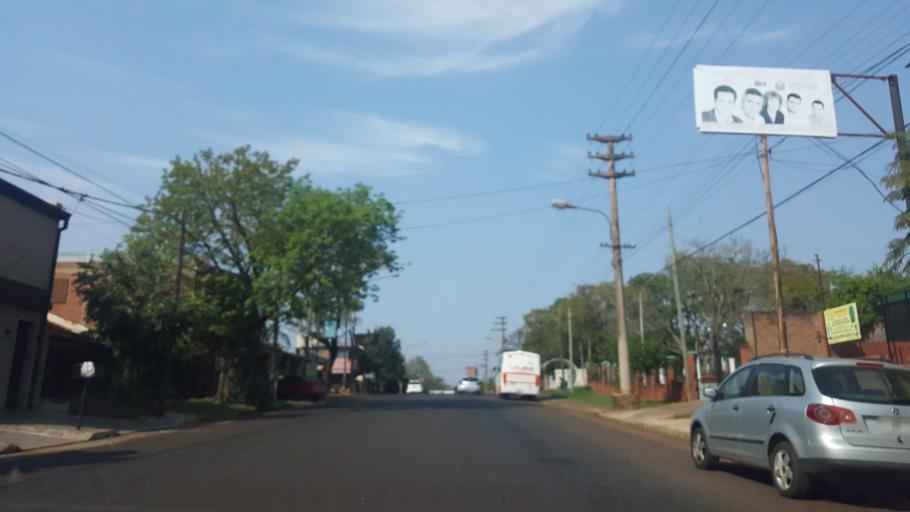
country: AR
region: Misiones
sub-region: Departamento de Capital
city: Posadas
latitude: -27.3816
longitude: -55.9034
